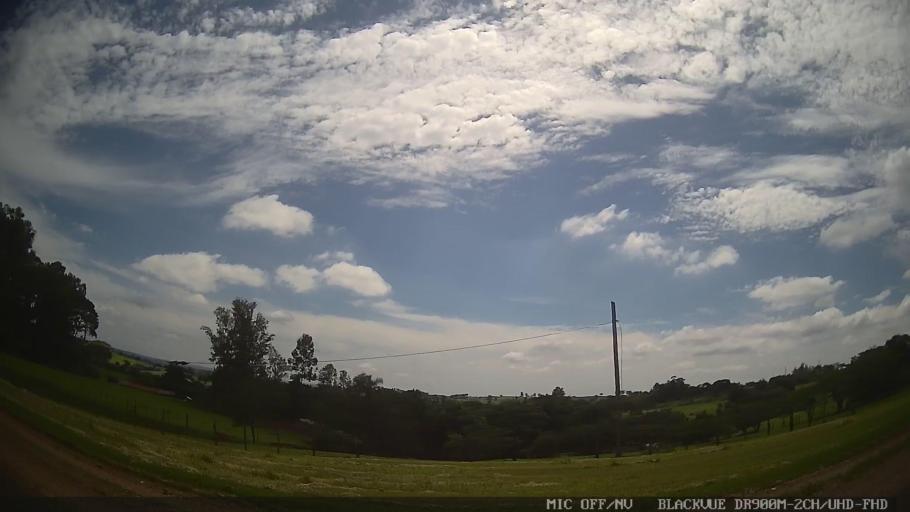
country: BR
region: Sao Paulo
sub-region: Laranjal Paulista
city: Laranjal Paulista
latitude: -23.0768
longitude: -47.8087
